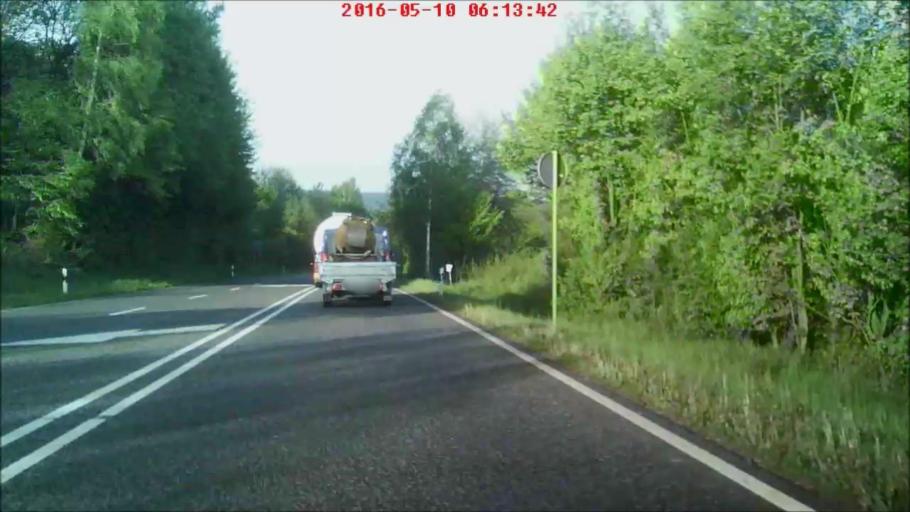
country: DE
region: Hesse
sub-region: Regierungsbezirk Kassel
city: Burghaun
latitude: 50.7655
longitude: 9.6928
